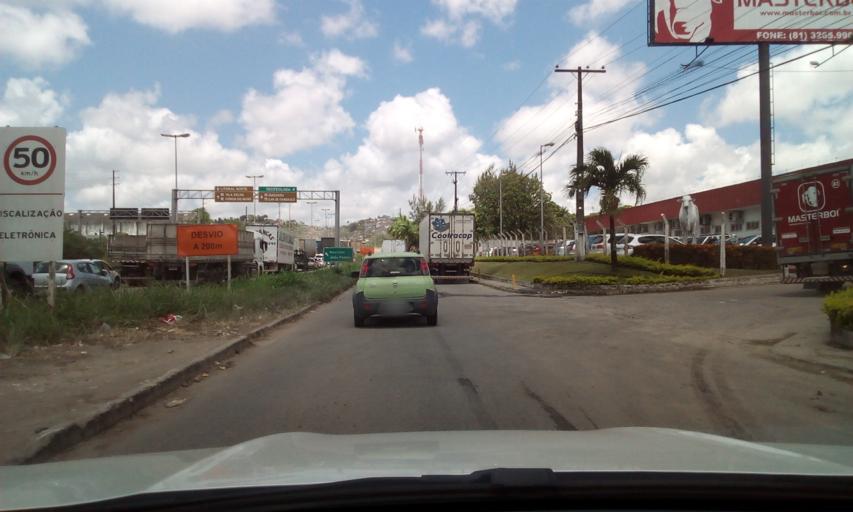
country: BR
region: Pernambuco
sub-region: Recife
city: Recife
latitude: -8.0136
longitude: -34.9387
